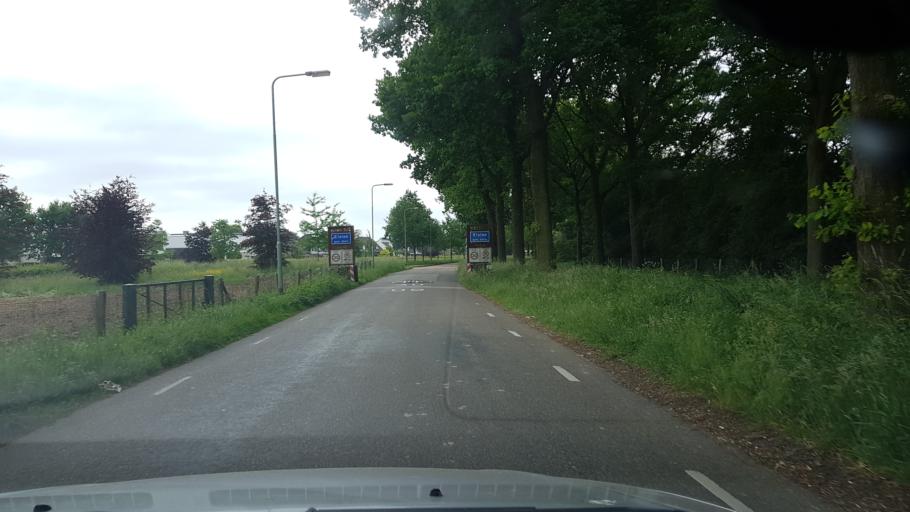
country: NL
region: Limburg
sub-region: Gemeente Stein
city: Elsloo
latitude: 50.9558
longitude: 5.7624
